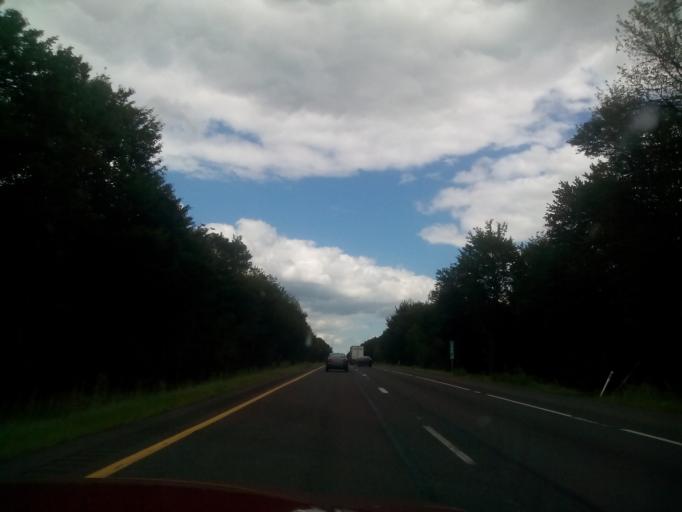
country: US
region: Pennsylvania
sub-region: Monroe County
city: Pocono Pines
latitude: 41.0738
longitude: -75.4657
